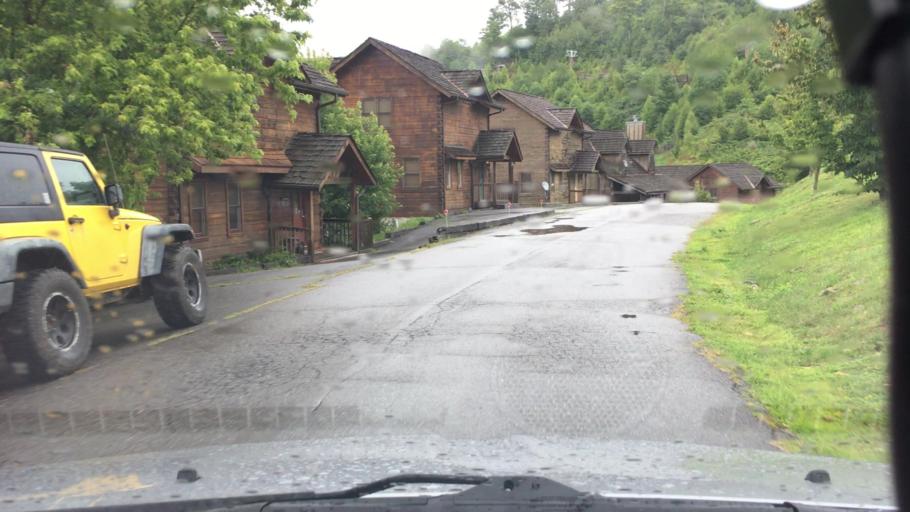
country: US
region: North Carolina
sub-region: Madison County
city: Mars Hill
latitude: 35.9486
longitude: -82.5132
